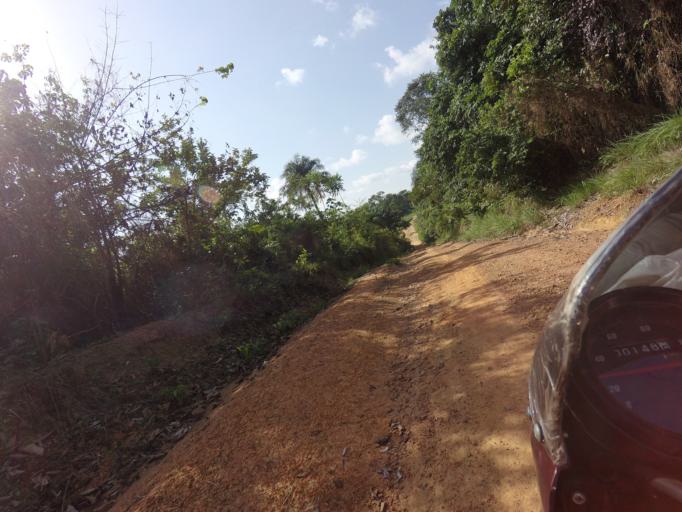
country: SL
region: Eastern Province
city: Kailahun
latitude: 8.3549
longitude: -10.7122
